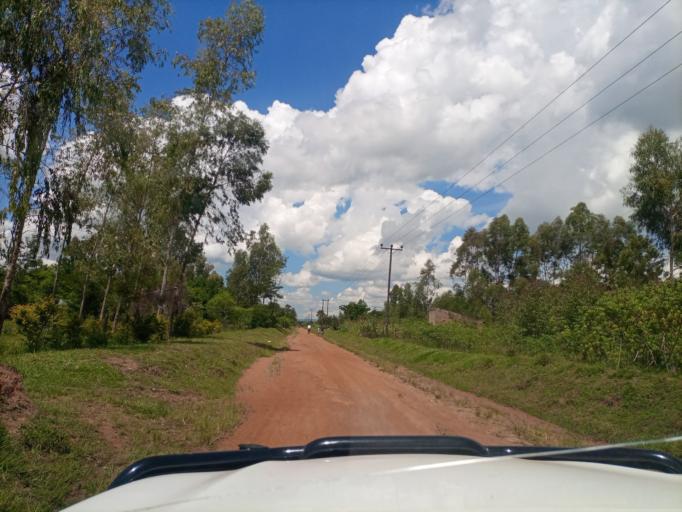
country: UG
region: Eastern Region
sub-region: Tororo District
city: Tororo
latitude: 0.6533
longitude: 33.9982
